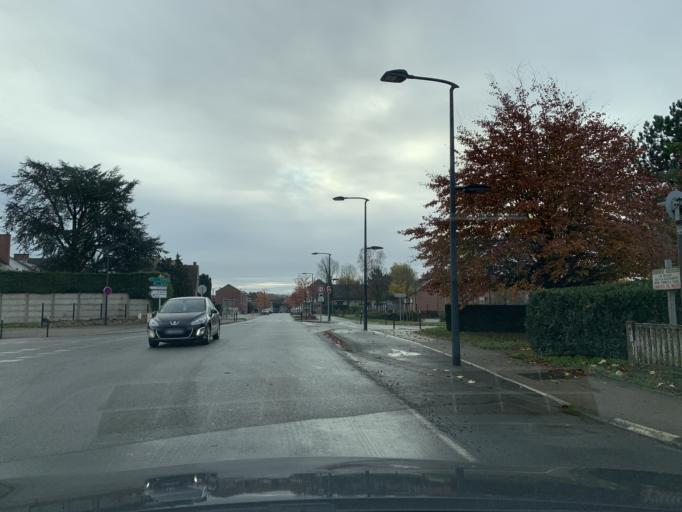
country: FR
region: Nord-Pas-de-Calais
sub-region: Departement du Nord
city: Cantin
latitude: 50.3132
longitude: 3.1225
